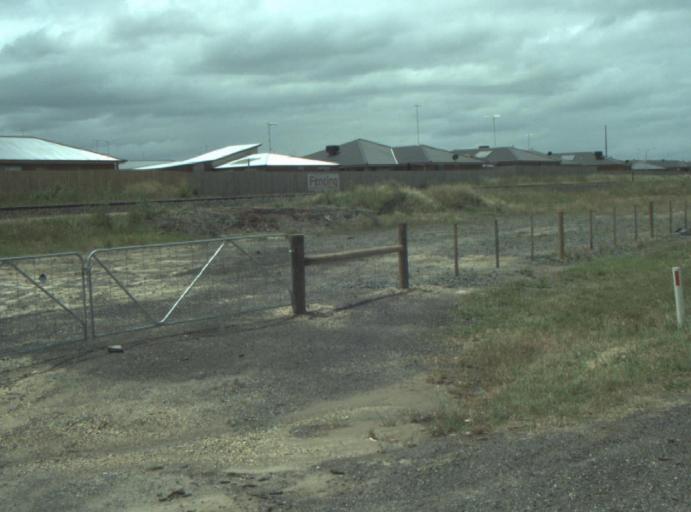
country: AU
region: Victoria
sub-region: Greater Geelong
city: Wandana Heights
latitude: -38.2171
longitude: 144.3012
